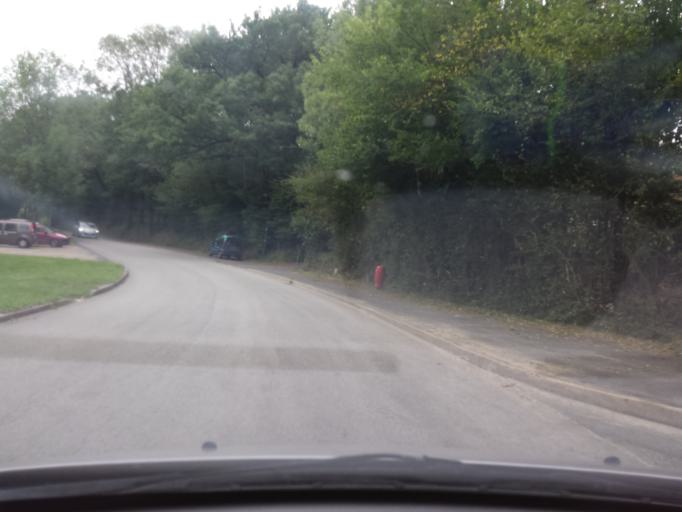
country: FR
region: Pays de la Loire
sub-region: Departement de la Vendee
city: Les Lucs-sur-Boulogne
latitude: 46.8479
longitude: -1.4877
